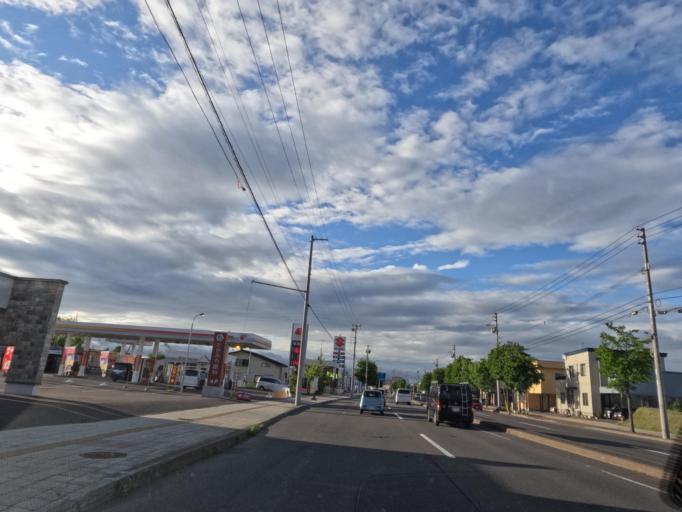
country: JP
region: Hokkaido
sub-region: Asahikawa-shi
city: Asahikawa
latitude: 43.7452
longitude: 142.3577
